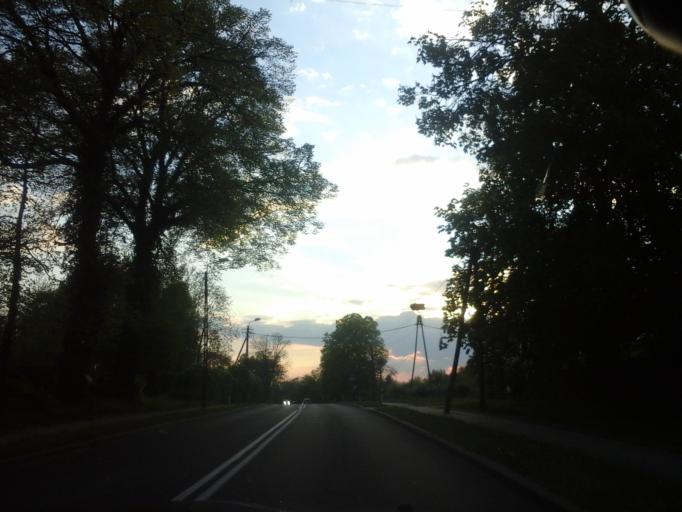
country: PL
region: West Pomeranian Voivodeship
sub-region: Powiat drawski
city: Kalisz Pomorski
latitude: 53.2962
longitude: 15.8407
